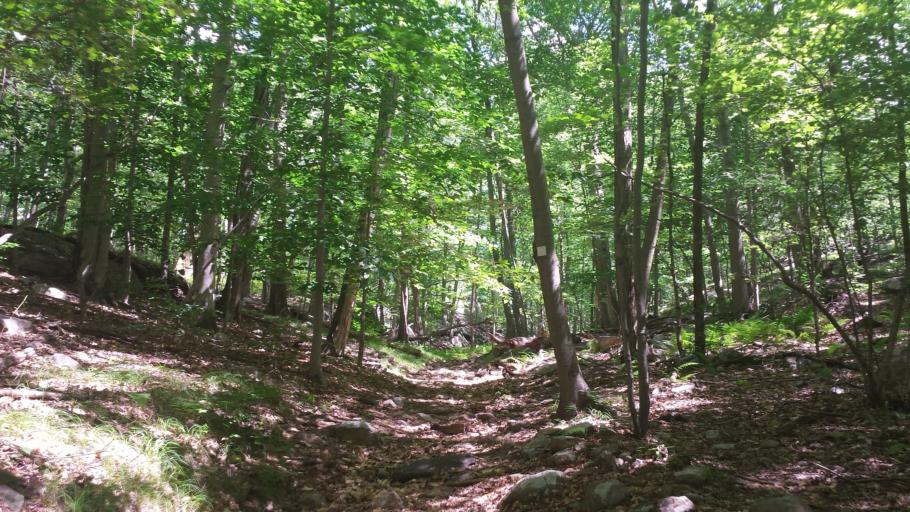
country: US
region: New York
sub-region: Westchester County
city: Pound Ridge
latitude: 41.2496
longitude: -73.5773
